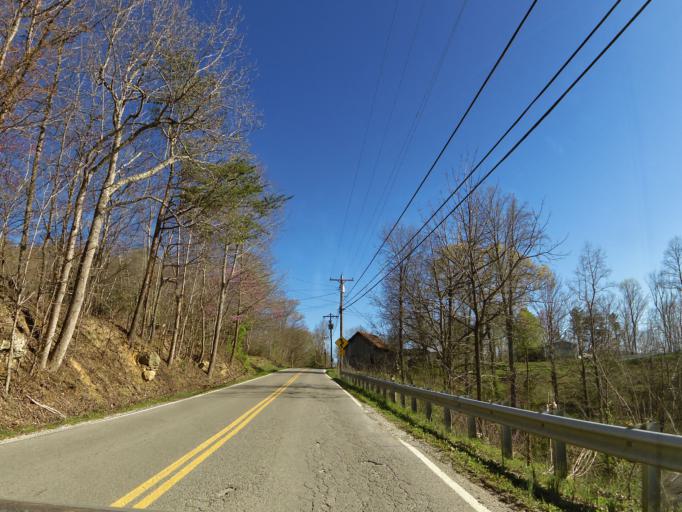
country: US
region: Tennessee
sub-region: Scott County
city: Huntsville
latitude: 36.3605
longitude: -84.3982
